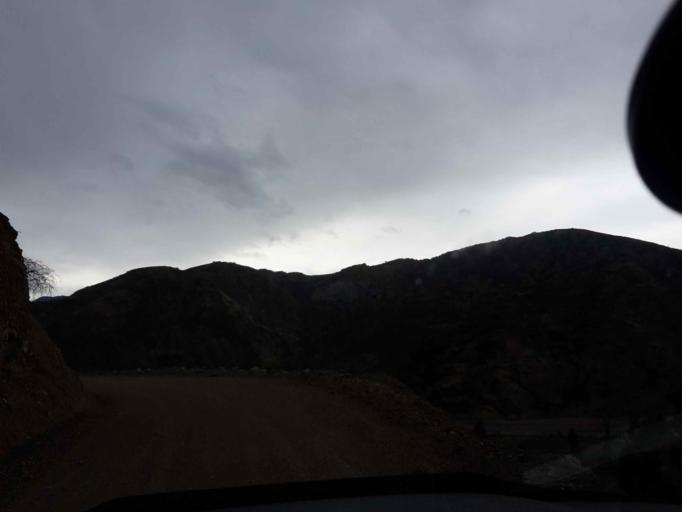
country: BO
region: Cochabamba
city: Sipe Sipe
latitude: -17.5278
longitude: -66.5281
